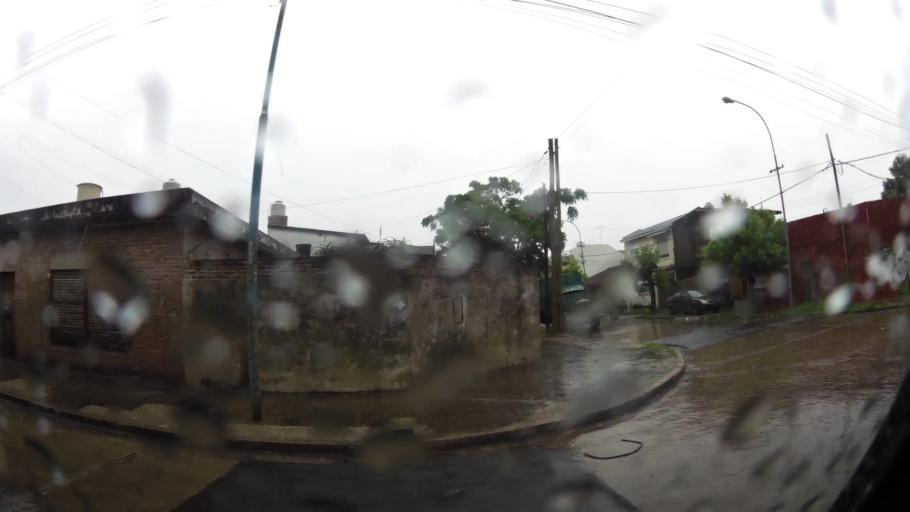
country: AR
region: Buenos Aires
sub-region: Partido de Lanus
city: Lanus
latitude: -34.7150
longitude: -58.4116
